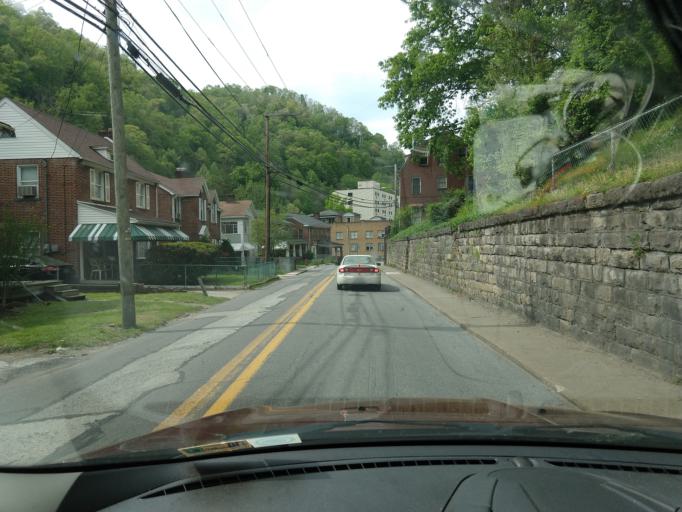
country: US
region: West Virginia
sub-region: McDowell County
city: Welch
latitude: 37.4287
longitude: -81.5849
